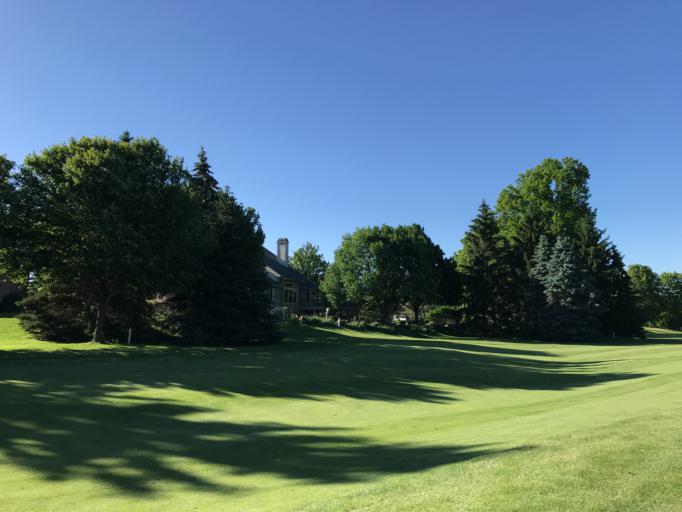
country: US
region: Michigan
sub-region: Oakland County
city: South Lyon
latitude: 42.4505
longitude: -83.5825
